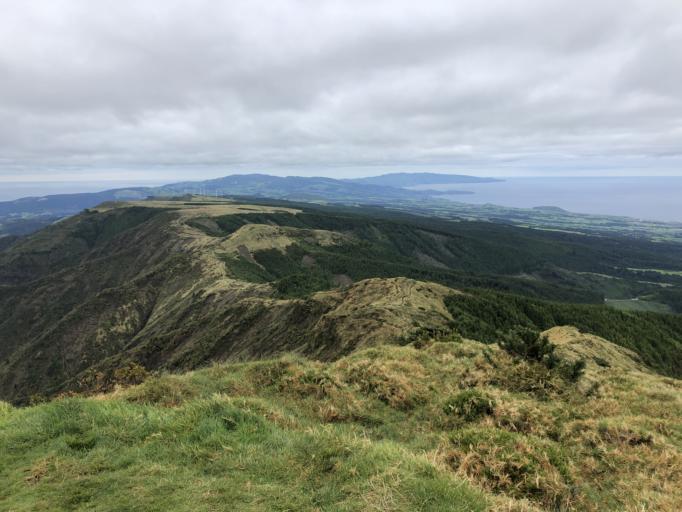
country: PT
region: Azores
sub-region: Povoacao
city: Furnas
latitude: 37.8096
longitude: -25.2112
